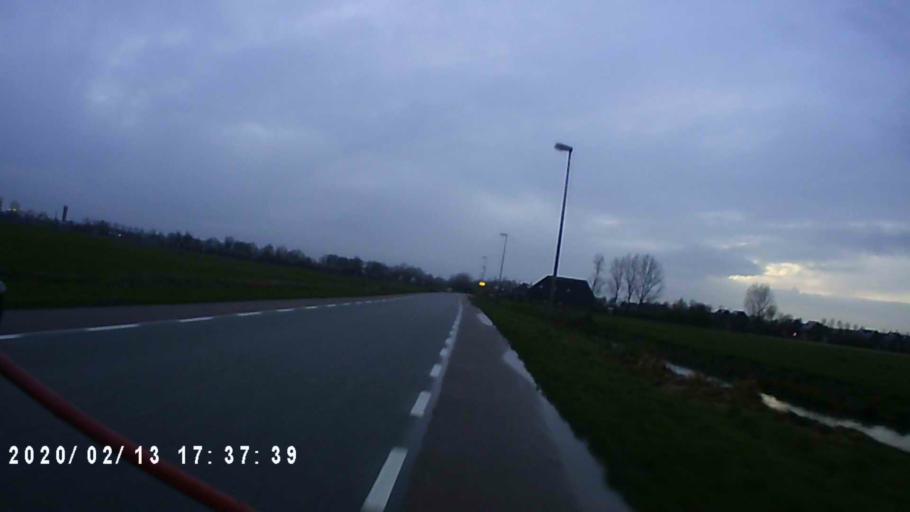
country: NL
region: Groningen
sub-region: Gemeente Zuidhorn
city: Aduard
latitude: 53.2275
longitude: 6.5075
